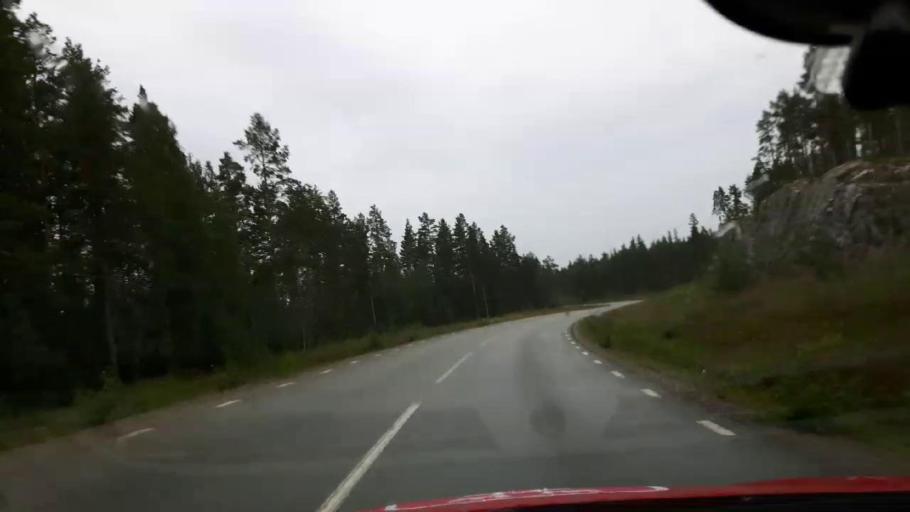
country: SE
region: Jaemtland
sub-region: OEstersunds Kommun
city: Brunflo
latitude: 62.8078
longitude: 14.9972
